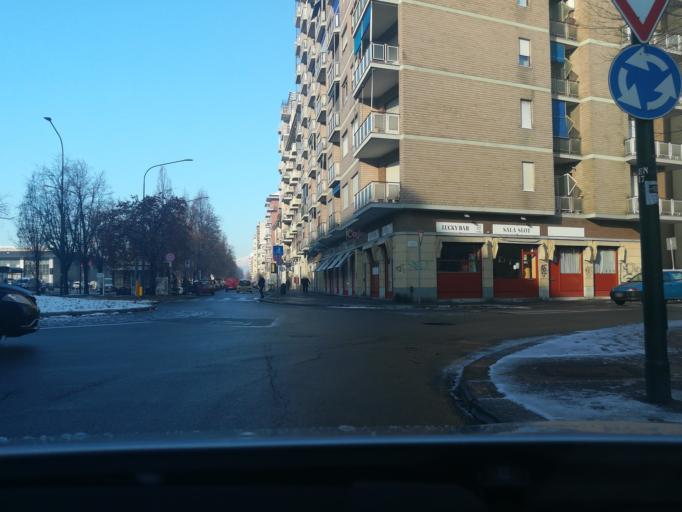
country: IT
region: Piedmont
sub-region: Provincia di Torino
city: Lesna
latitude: 45.0557
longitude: 7.6451
